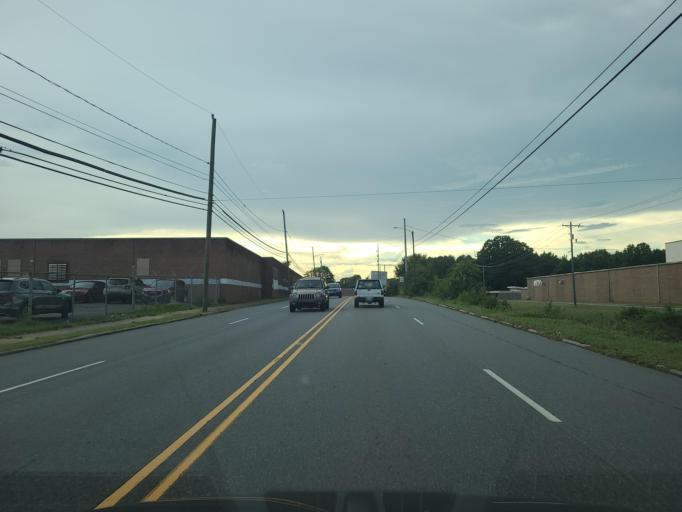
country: US
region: North Carolina
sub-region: Gaston County
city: Ranlo
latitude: 35.2783
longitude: -81.1249
